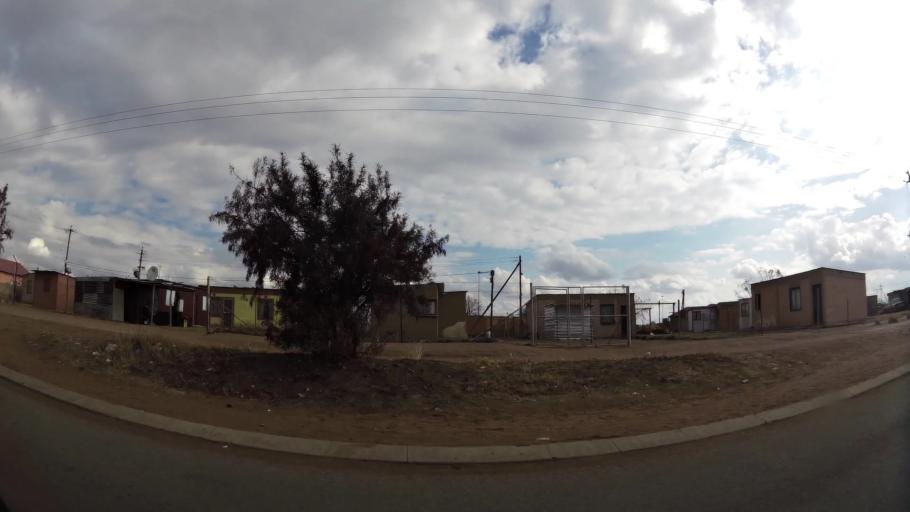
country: ZA
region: Gauteng
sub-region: Sedibeng District Municipality
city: Vanderbijlpark
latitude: -26.6833
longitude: 27.7821
